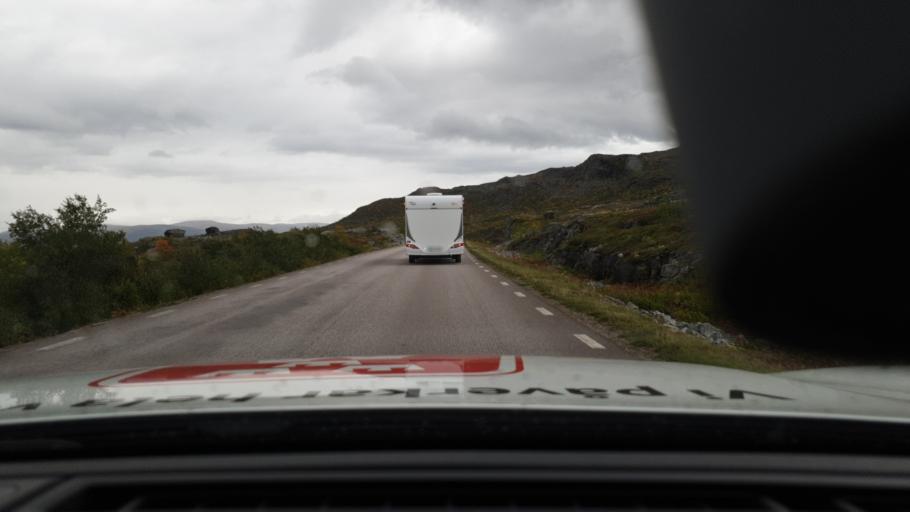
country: NO
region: Troms
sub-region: Bardu
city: Setermoen
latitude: 68.4321
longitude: 18.5352
